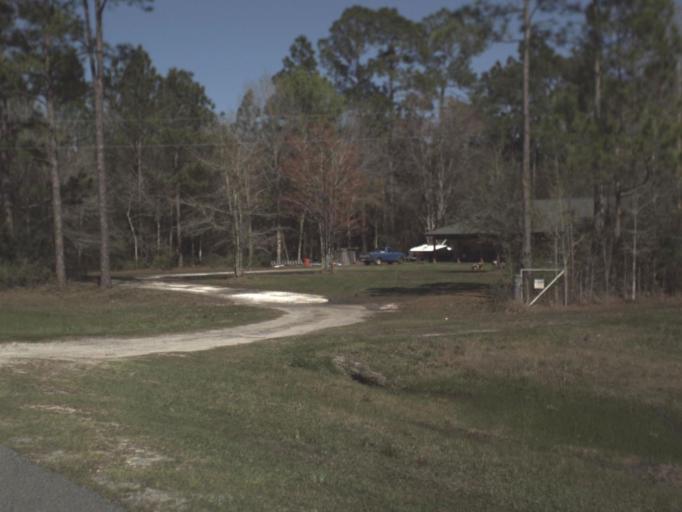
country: US
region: Florida
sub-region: Gulf County
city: Port Saint Joe
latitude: 29.8911
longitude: -85.2163
